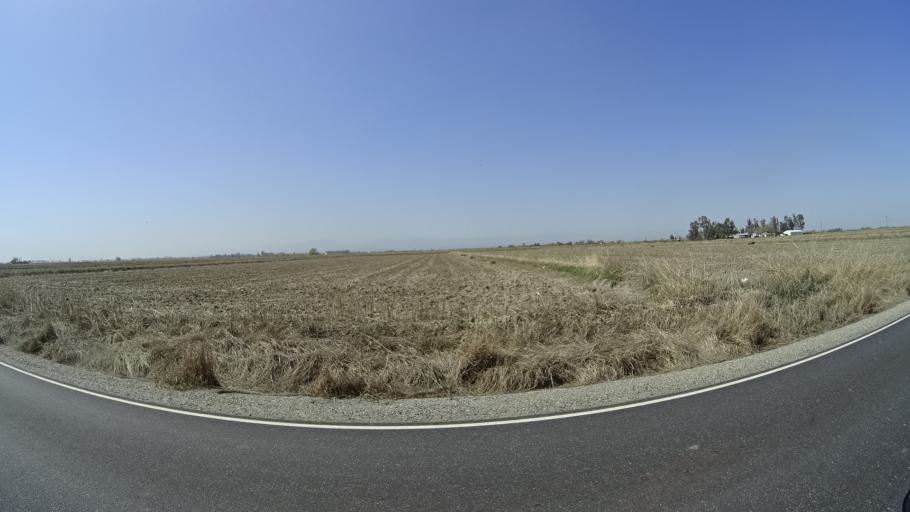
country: US
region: California
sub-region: Glenn County
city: Willows
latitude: 39.5503
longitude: -122.1365
